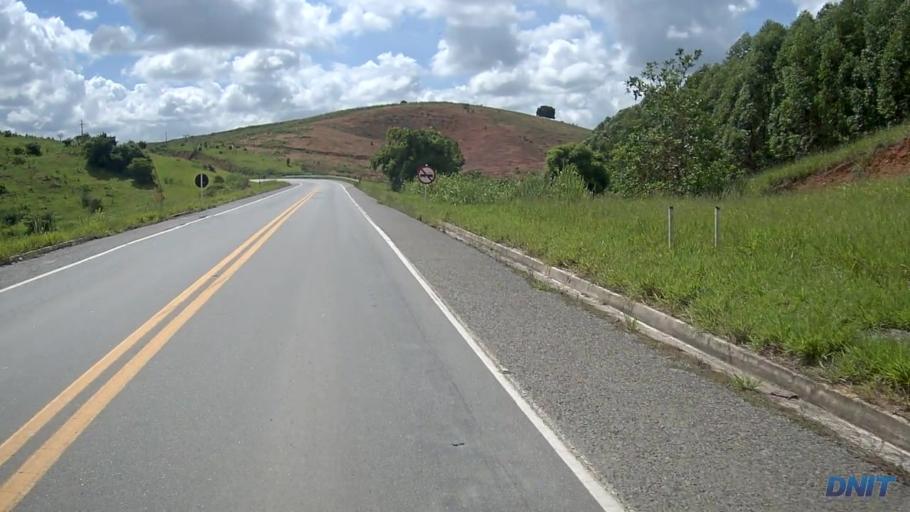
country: BR
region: Minas Gerais
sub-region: Governador Valadares
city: Governador Valadares
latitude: -19.0665
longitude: -42.1679
